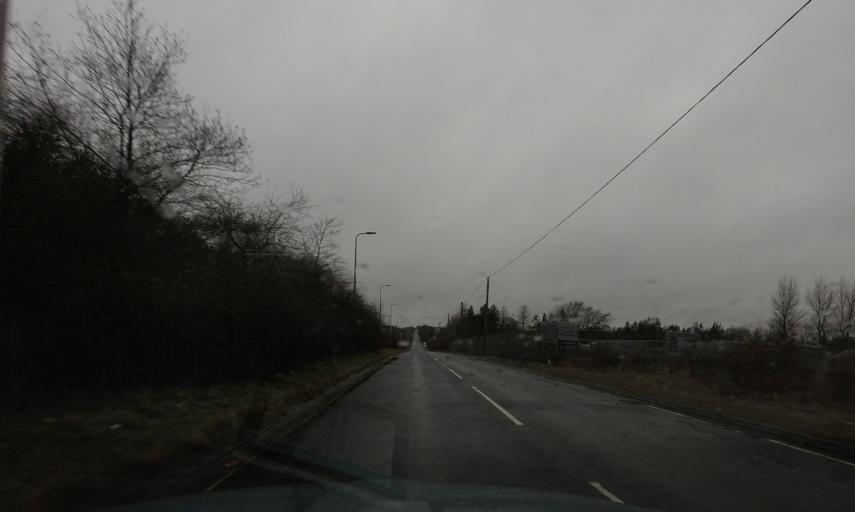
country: GB
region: Scotland
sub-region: North Lanarkshire
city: Shotts
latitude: 55.8555
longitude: -3.7909
